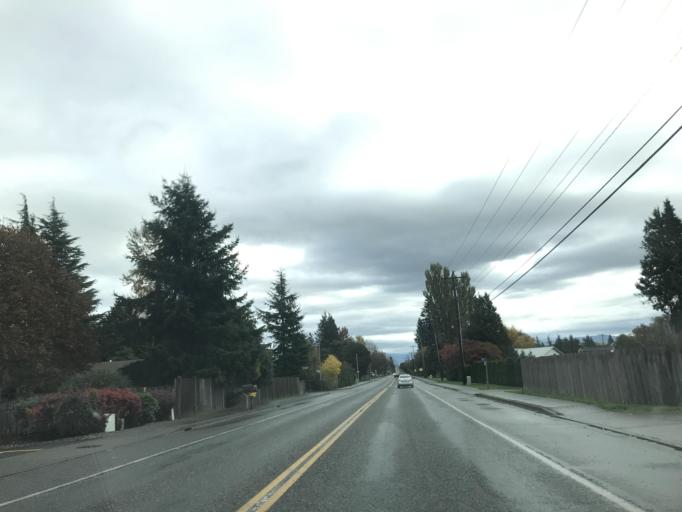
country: US
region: Washington
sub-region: Whatcom County
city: Ferndale
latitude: 48.8334
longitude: -122.5493
